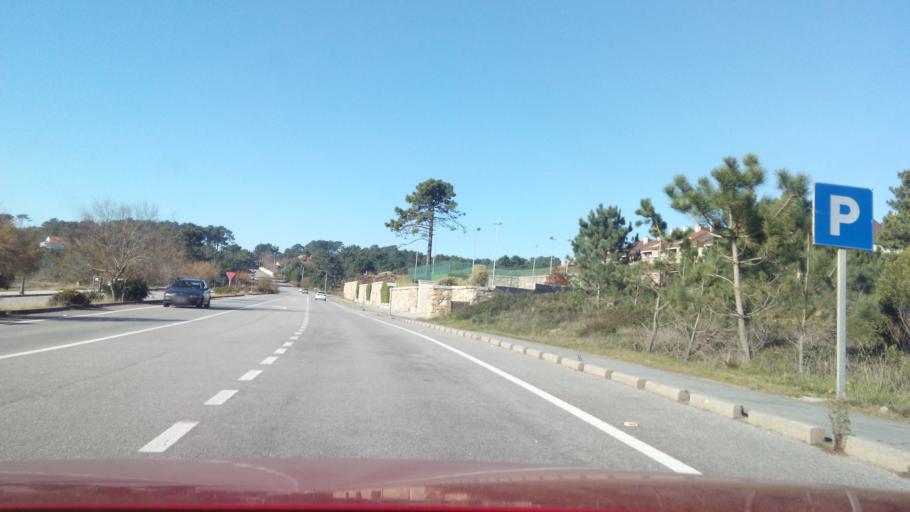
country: ES
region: Galicia
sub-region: Provincia de Pontevedra
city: O Grove
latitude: 42.4617
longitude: -8.8967
